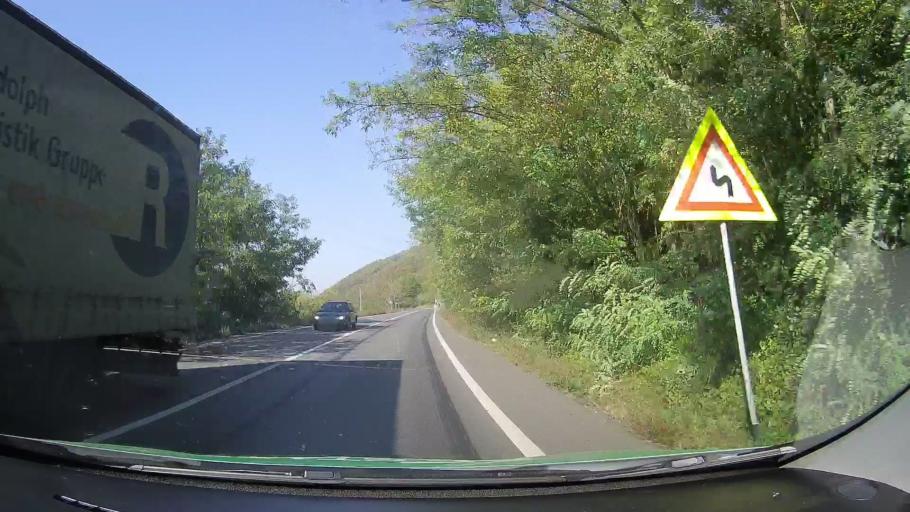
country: RO
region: Arad
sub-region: Comuna Savarsin
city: Savarsin
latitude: 45.9971
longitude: 22.2919
